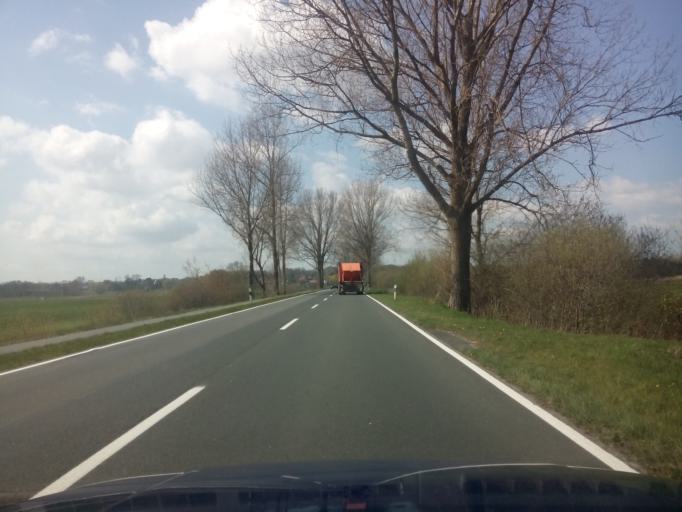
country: DE
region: Lower Saxony
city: Osterholz-Scharmbeck
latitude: 53.2140
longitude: 8.8137
